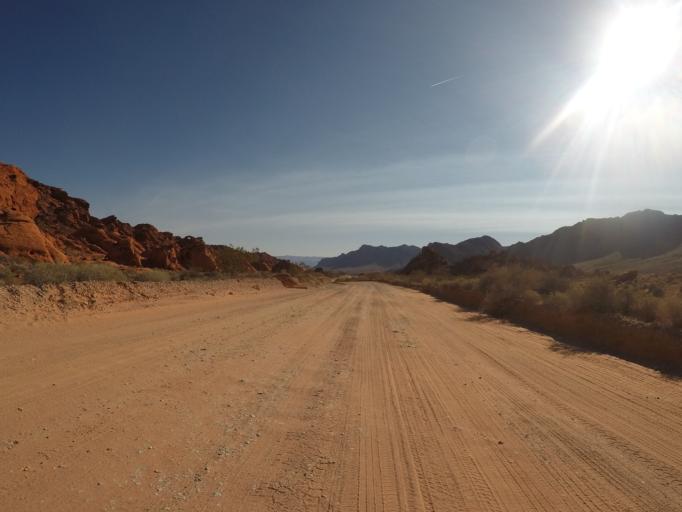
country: US
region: Nevada
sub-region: Clark County
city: Moapa Valley
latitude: 36.4122
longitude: -114.5555
